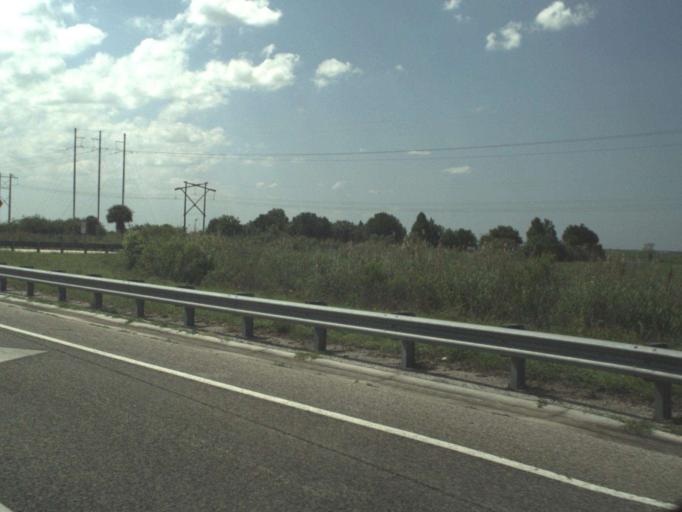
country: US
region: Florida
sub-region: Brevard County
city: Cocoa West
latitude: 28.3694
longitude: -80.8693
